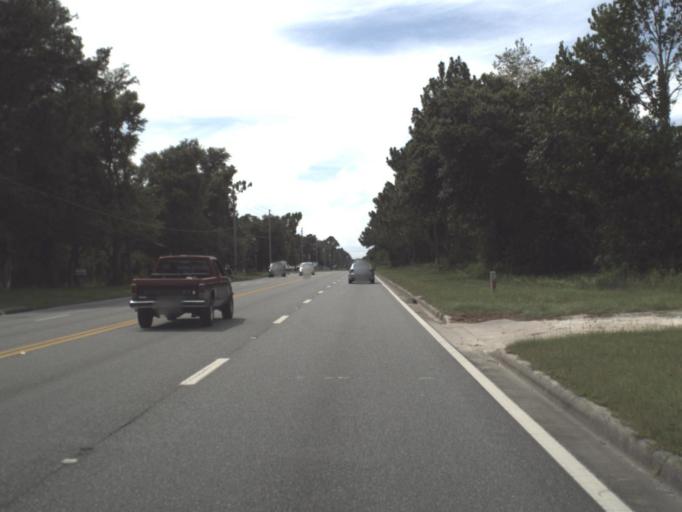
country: US
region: Florida
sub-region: Taylor County
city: Perry
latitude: 30.0994
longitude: -83.5526
